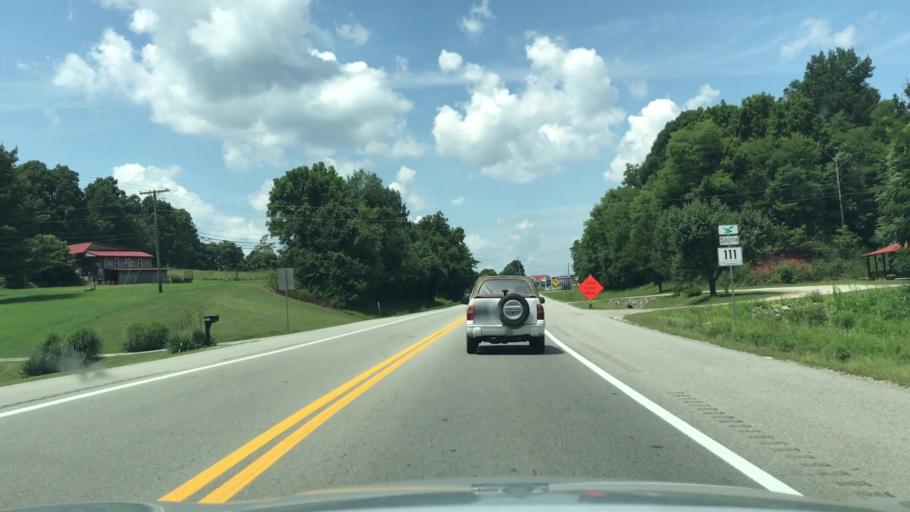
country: US
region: Tennessee
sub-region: Pickett County
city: Byrdstown
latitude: 36.5724
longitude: -85.1572
